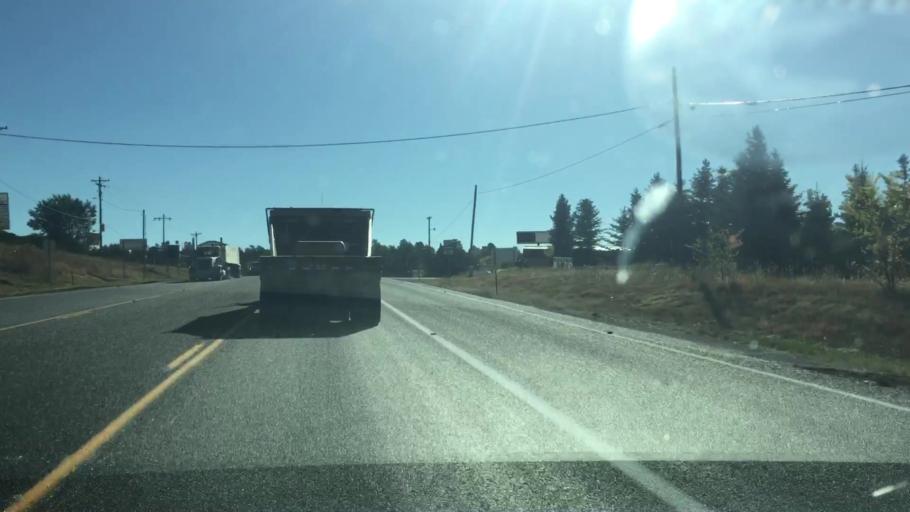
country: US
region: Colorado
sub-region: Douglas County
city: The Pinery
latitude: 39.3908
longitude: -104.7516
